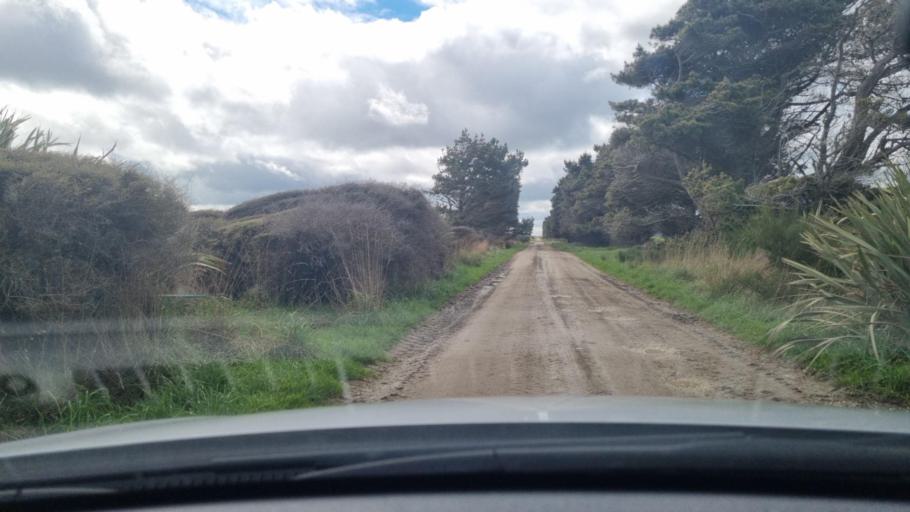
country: NZ
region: Southland
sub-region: Invercargill City
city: Bluff
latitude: -46.5712
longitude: 168.4987
